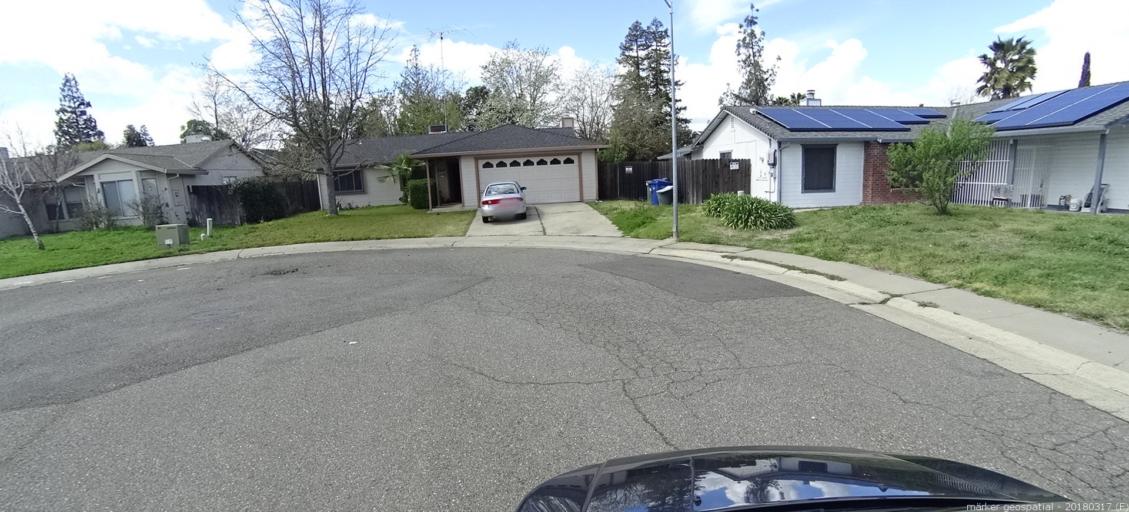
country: US
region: California
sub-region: Sacramento County
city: Florin
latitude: 38.4798
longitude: -121.4033
